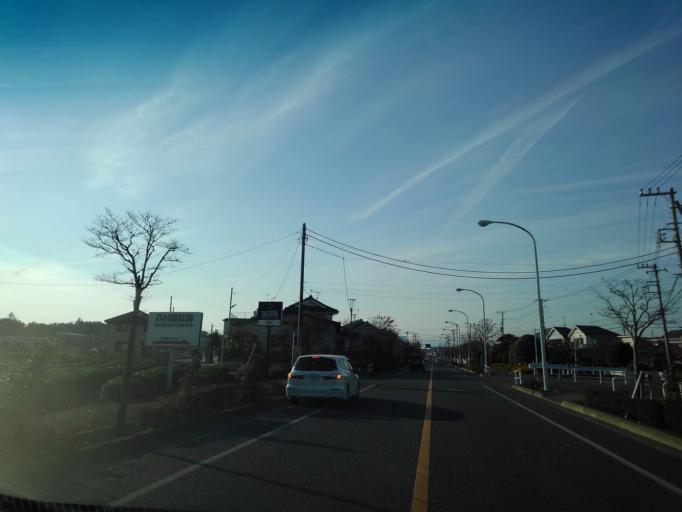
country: JP
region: Tokyo
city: Fussa
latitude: 35.7915
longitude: 139.3593
